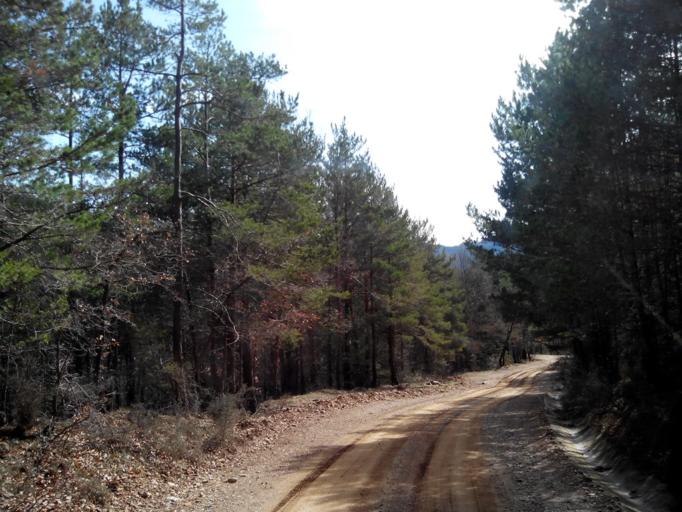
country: ES
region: Catalonia
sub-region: Provincia de Barcelona
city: Vilada
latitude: 42.1541
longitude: 1.9305
